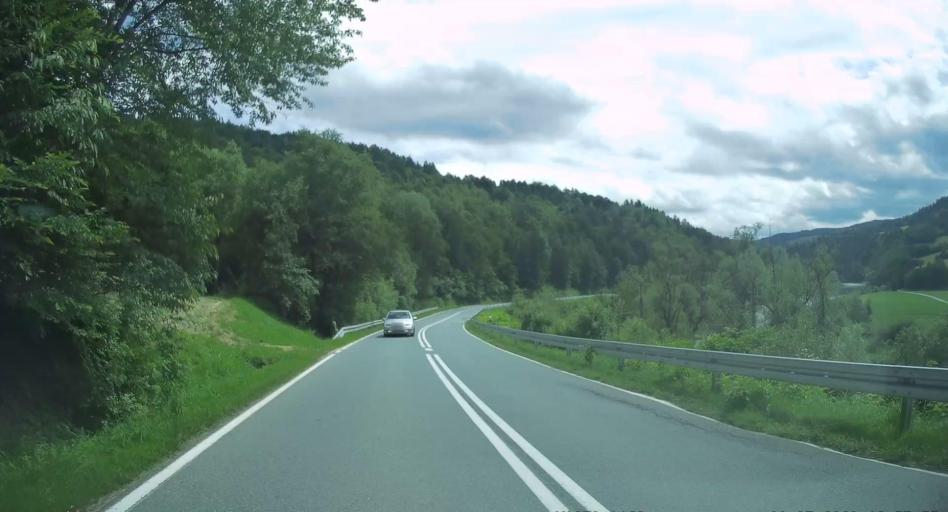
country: PL
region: Lesser Poland Voivodeship
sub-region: Powiat nowosadecki
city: Piwniczna-Zdroj
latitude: 49.3850
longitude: 20.7623
